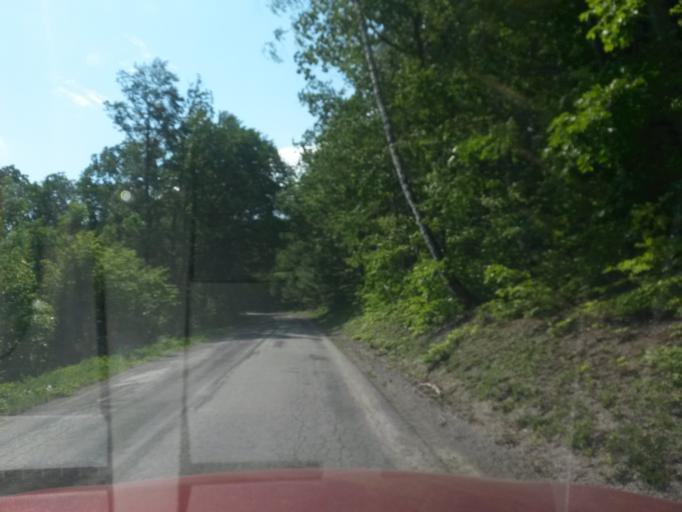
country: SK
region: Kosicky
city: Moldava nad Bodvou
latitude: 48.7238
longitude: 21.0363
